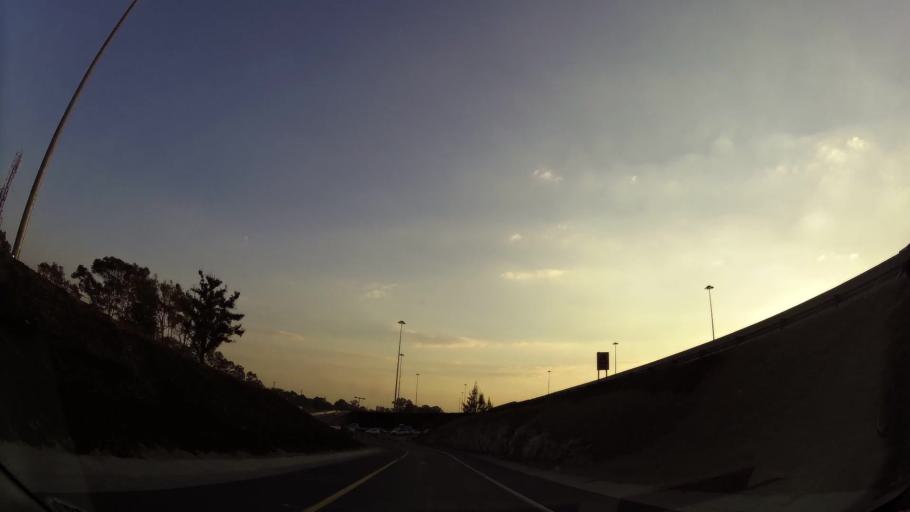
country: ZA
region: Gauteng
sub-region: Ekurhuleni Metropolitan Municipality
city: Benoni
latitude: -26.1757
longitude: 28.3349
